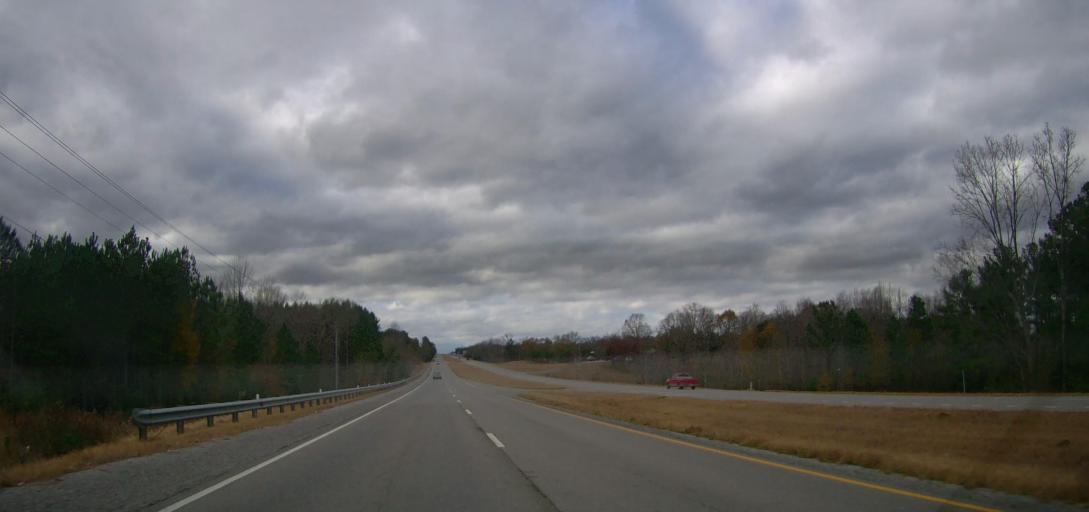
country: US
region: Alabama
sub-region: Lawrence County
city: Town Creek
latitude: 34.5806
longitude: -87.4105
